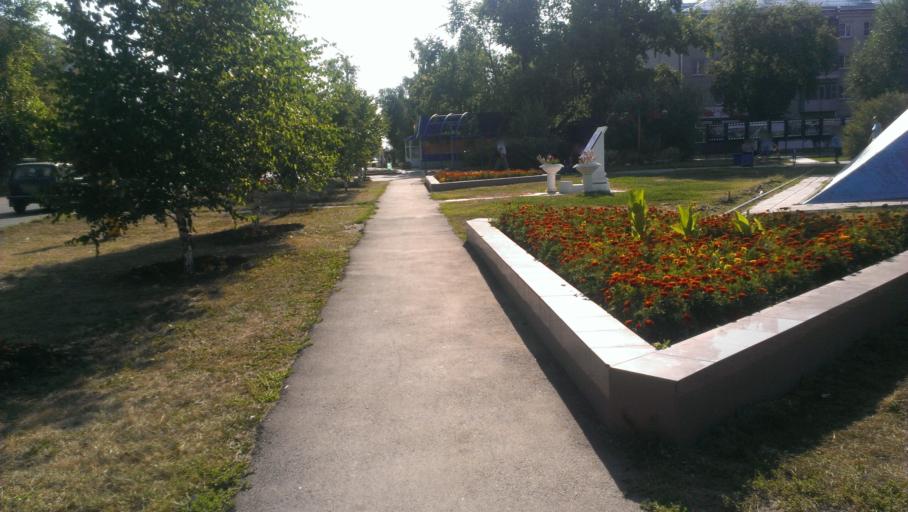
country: RU
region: Altai Krai
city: Novosilikatnyy
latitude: 53.3079
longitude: 83.6212
